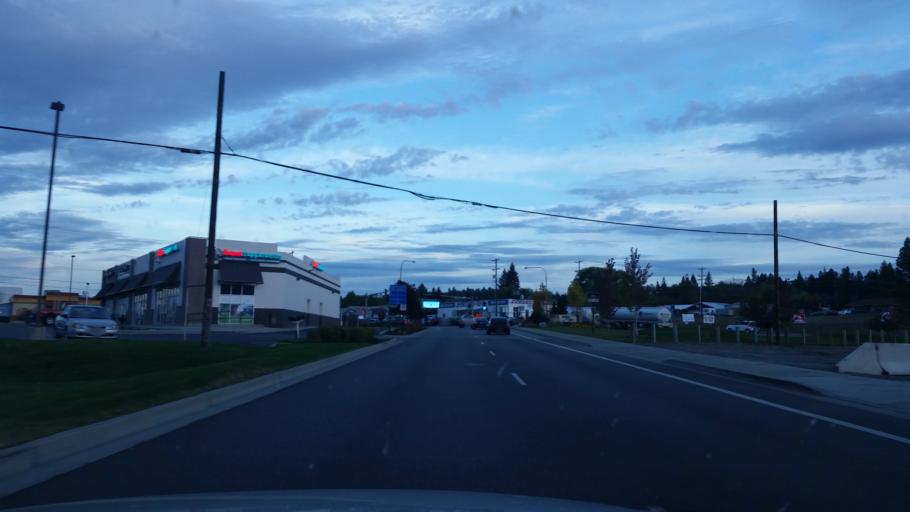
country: US
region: Washington
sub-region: Spokane County
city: Dishman
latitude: 47.6567
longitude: -117.3166
